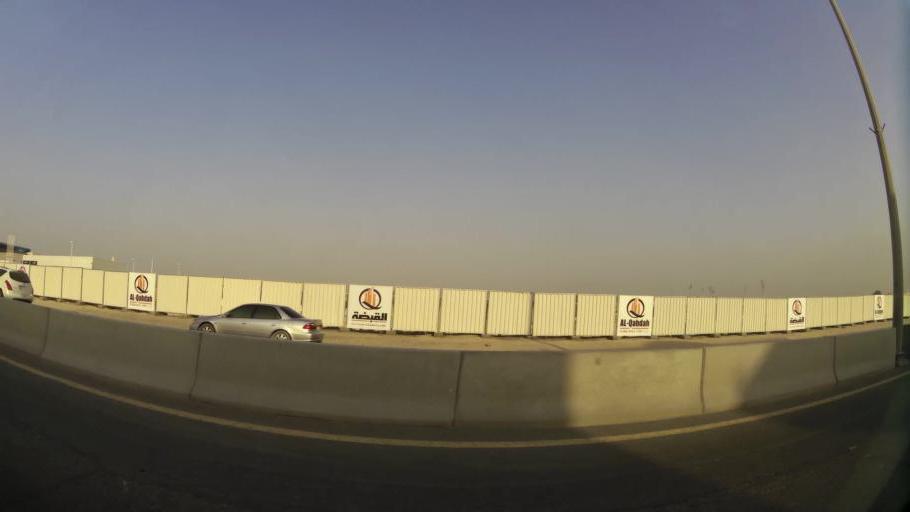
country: AE
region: Ash Shariqah
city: Sharjah
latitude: 25.3404
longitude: 55.4168
